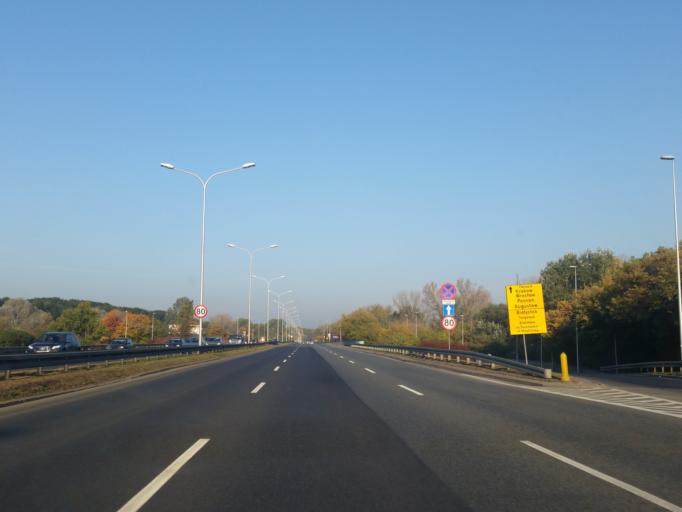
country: PL
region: Masovian Voivodeship
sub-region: Warszawa
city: Zoliborz
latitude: 52.2903
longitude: 20.9776
